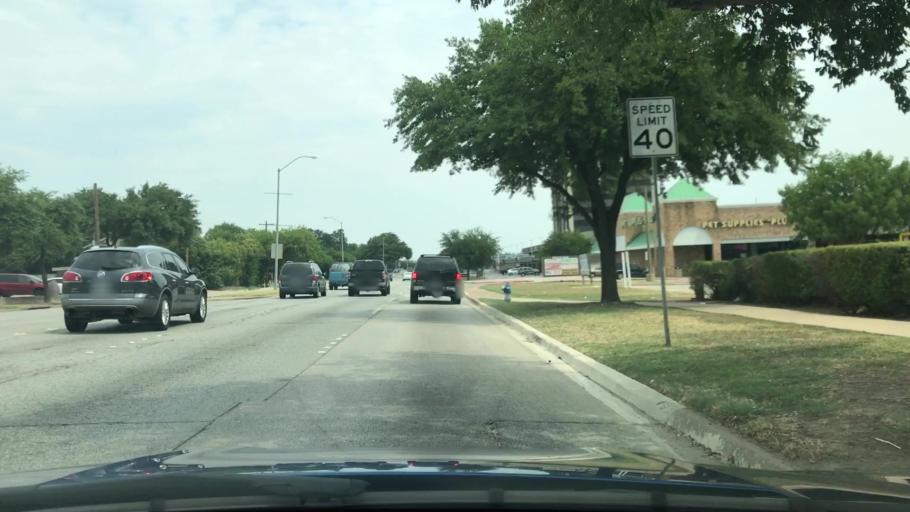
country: US
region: Texas
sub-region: Dallas County
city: Richardson
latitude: 32.9527
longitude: -96.7688
